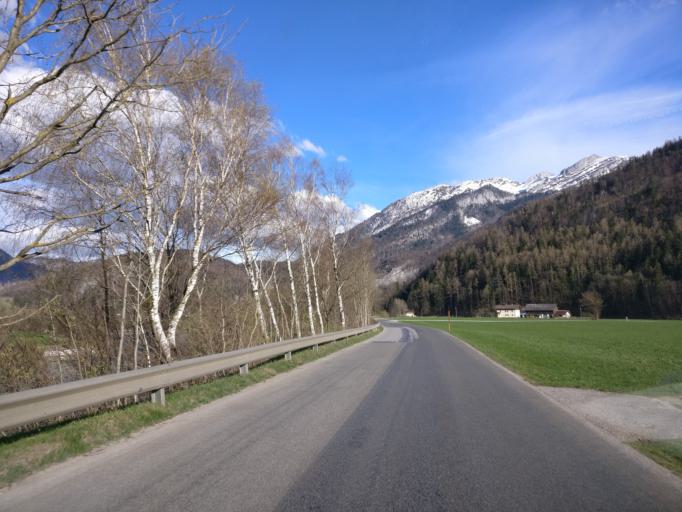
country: AT
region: Salzburg
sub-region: Politischer Bezirk Hallein
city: Golling an der Salzach
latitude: 47.5828
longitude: 13.1627
